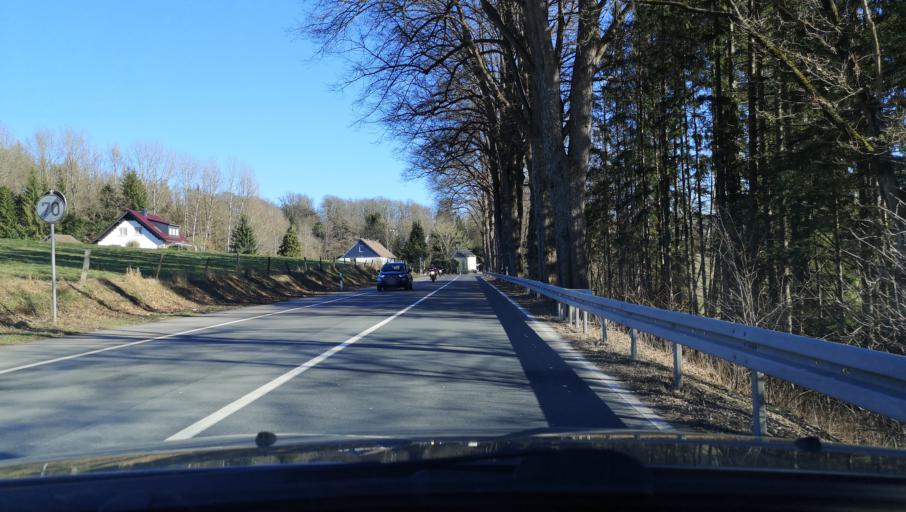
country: DE
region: North Rhine-Westphalia
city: Wipperfurth
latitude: 51.1164
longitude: 7.4567
